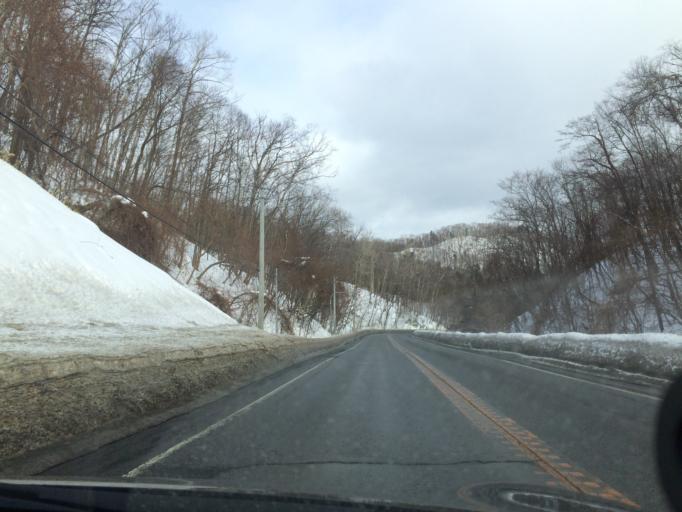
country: JP
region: Hokkaido
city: Shimo-furano
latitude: 42.8894
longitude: 142.2393
